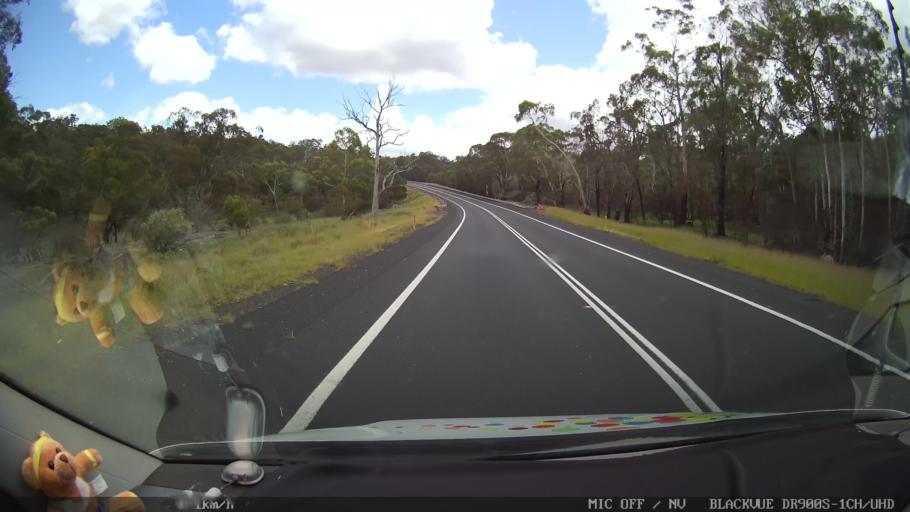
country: AU
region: New South Wales
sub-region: Glen Innes Severn
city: Glen Innes
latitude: -29.3543
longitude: 151.8974
